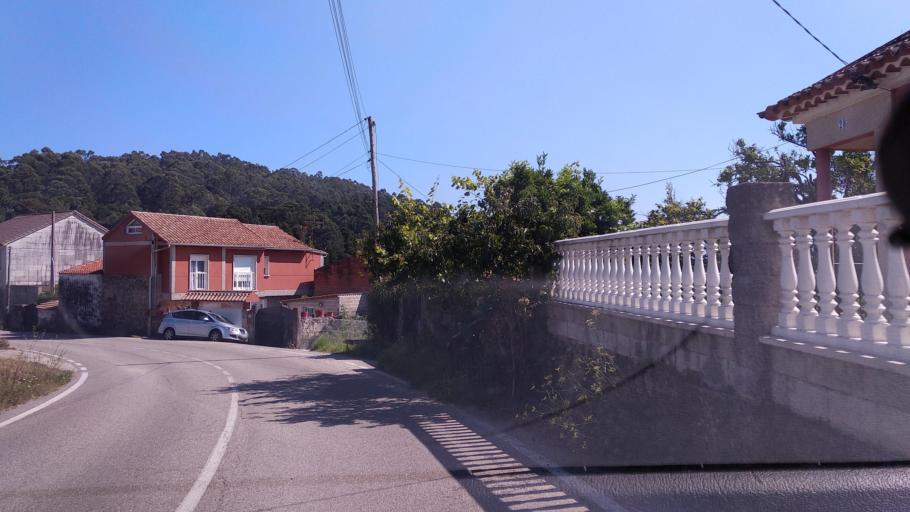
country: ES
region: Galicia
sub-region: Provincia de Pontevedra
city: Moana
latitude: 42.2760
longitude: -8.7619
